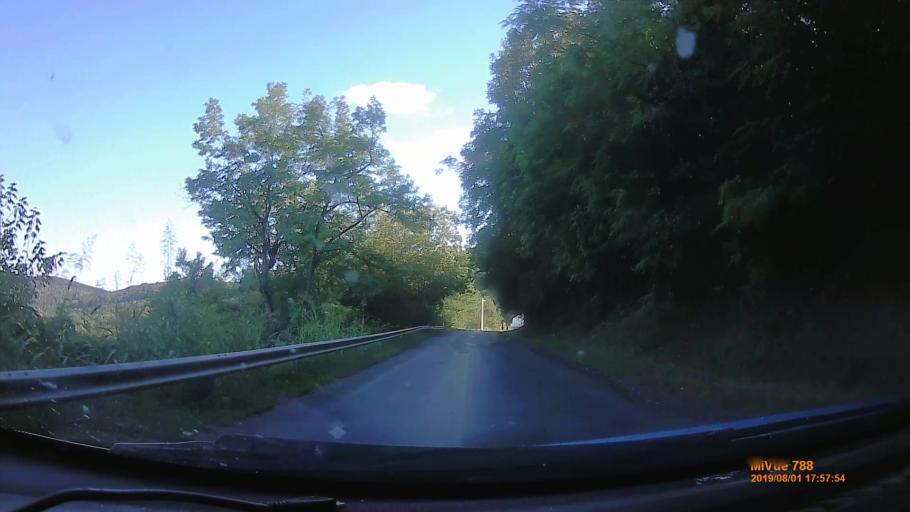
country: HU
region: Baranya
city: Sasd
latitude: 46.2010
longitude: 18.1142
